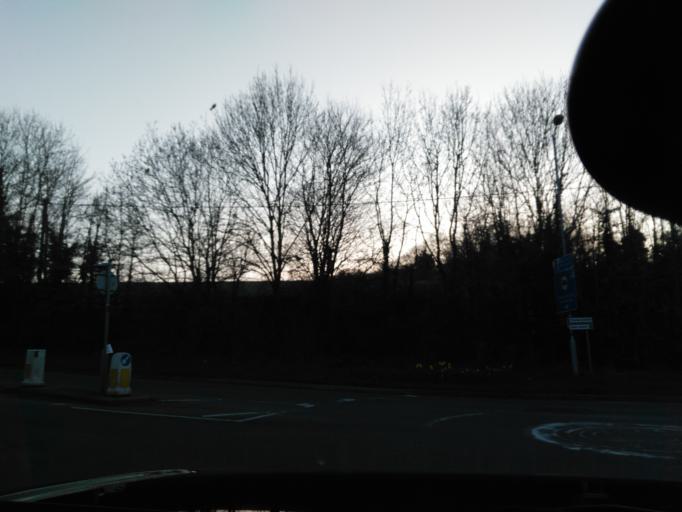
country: GB
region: England
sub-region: Wiltshire
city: Bradford-on-Avon
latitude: 51.3377
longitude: -2.2530
